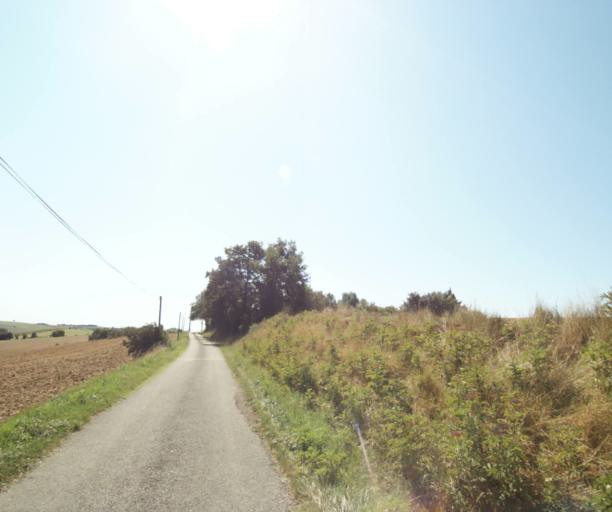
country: FR
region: Midi-Pyrenees
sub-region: Departement de l'Ariege
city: Lezat-sur-Leze
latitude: 43.2605
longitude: 1.3888
